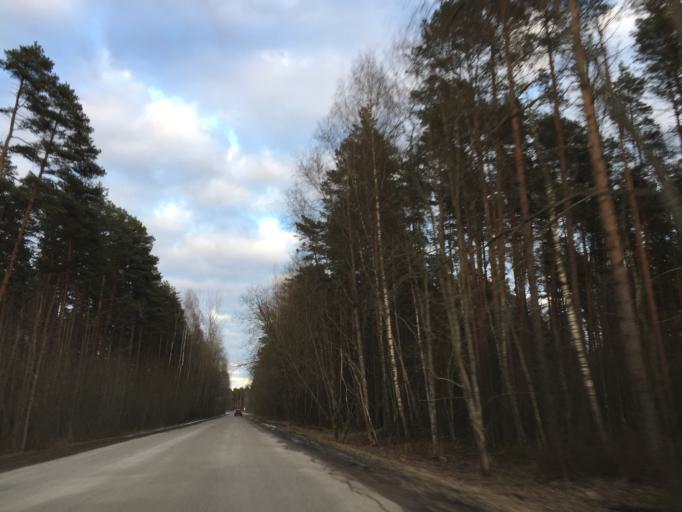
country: LV
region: Babite
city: Pinki
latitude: 56.9215
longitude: 23.8894
